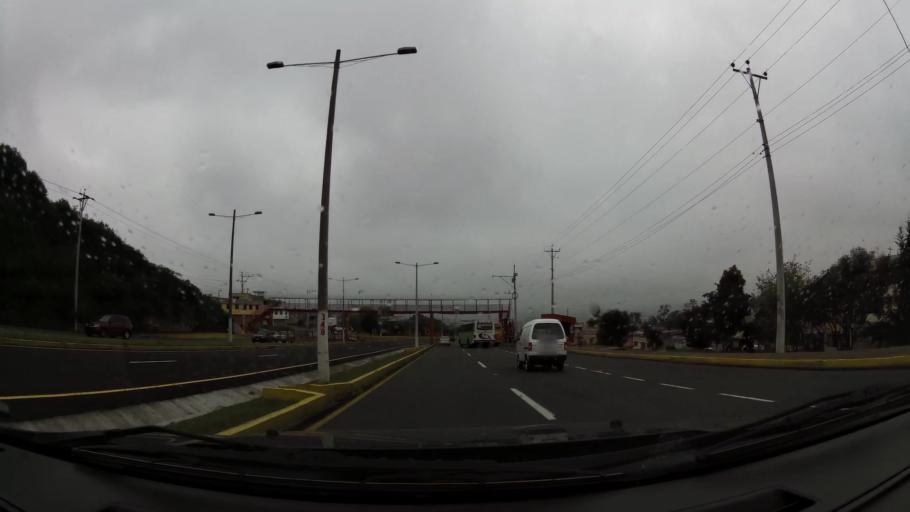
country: EC
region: Pichincha
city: Sangolqui
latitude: -0.2797
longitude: -78.4751
